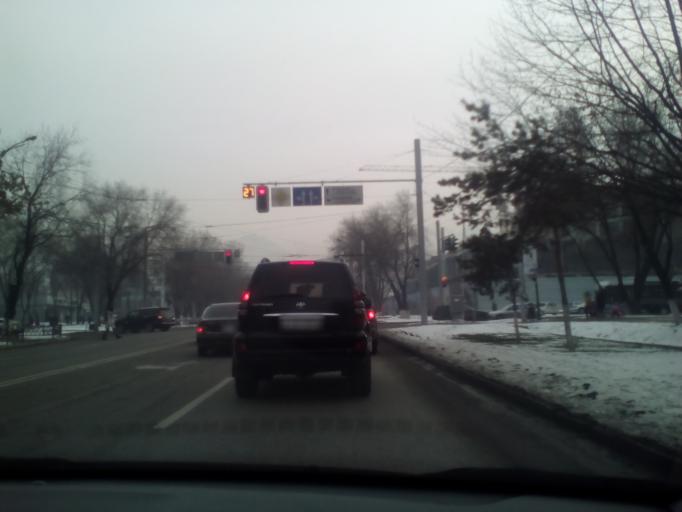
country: KZ
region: Almaty Qalasy
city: Almaty
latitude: 43.2335
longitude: 76.8319
